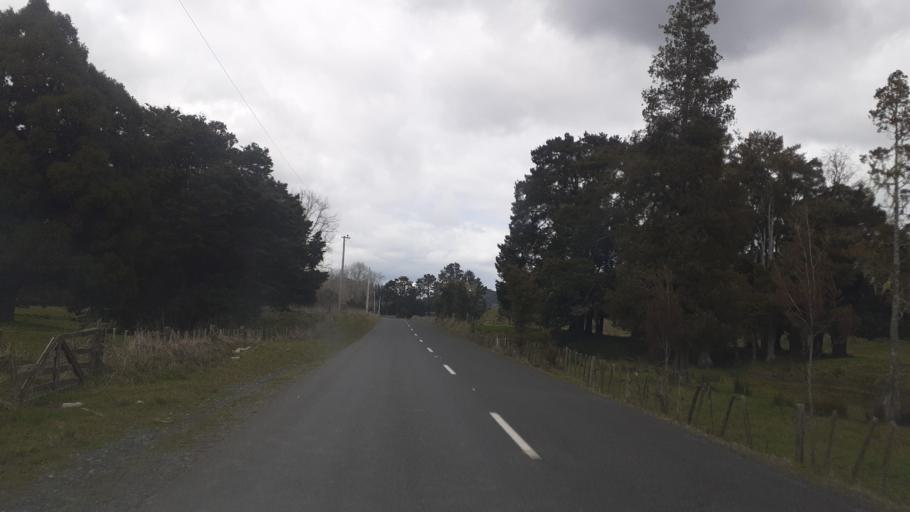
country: NZ
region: Northland
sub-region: Far North District
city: Moerewa
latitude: -35.5795
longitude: 173.9699
